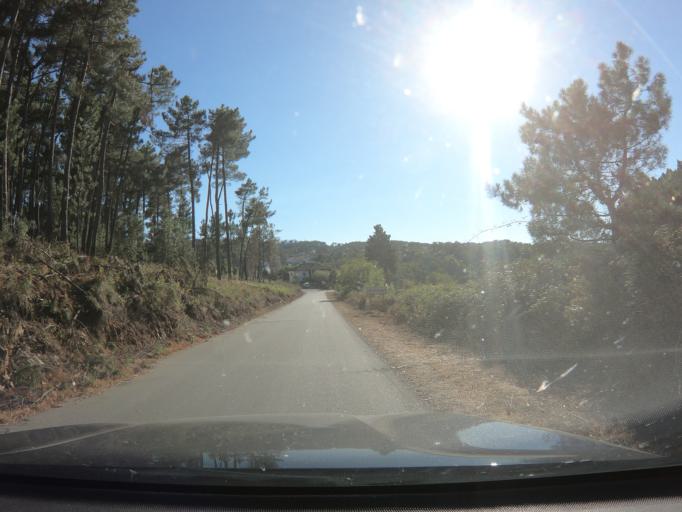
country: PT
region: Vila Real
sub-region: Sabrosa
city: Vilela
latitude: 41.2407
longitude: -7.6124
